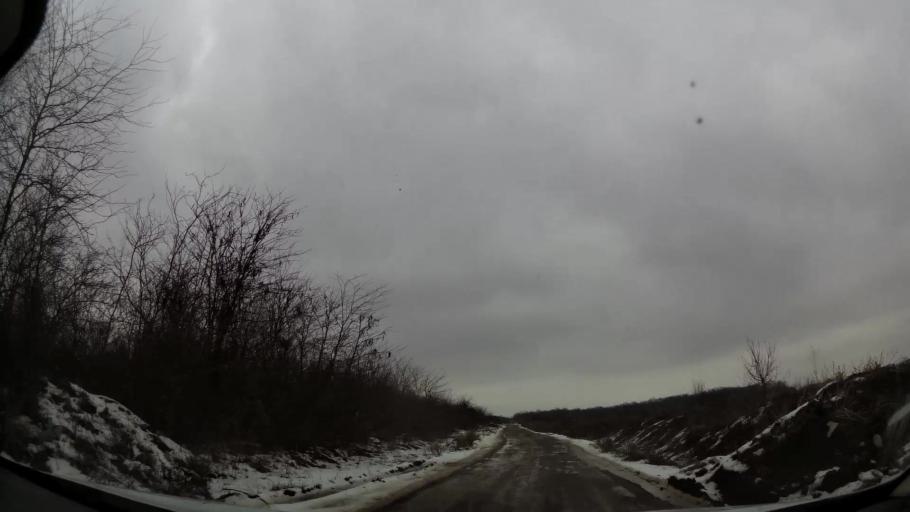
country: RO
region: Ilfov
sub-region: Comuna Chitila
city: Chitila
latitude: 44.5035
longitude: 26.0076
